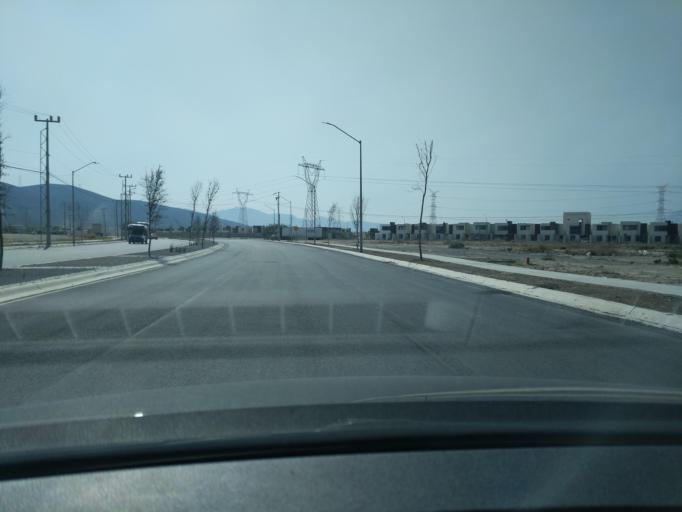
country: MX
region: Nuevo Leon
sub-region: Garcia
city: Los Parques
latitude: 25.7818
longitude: -100.4957
